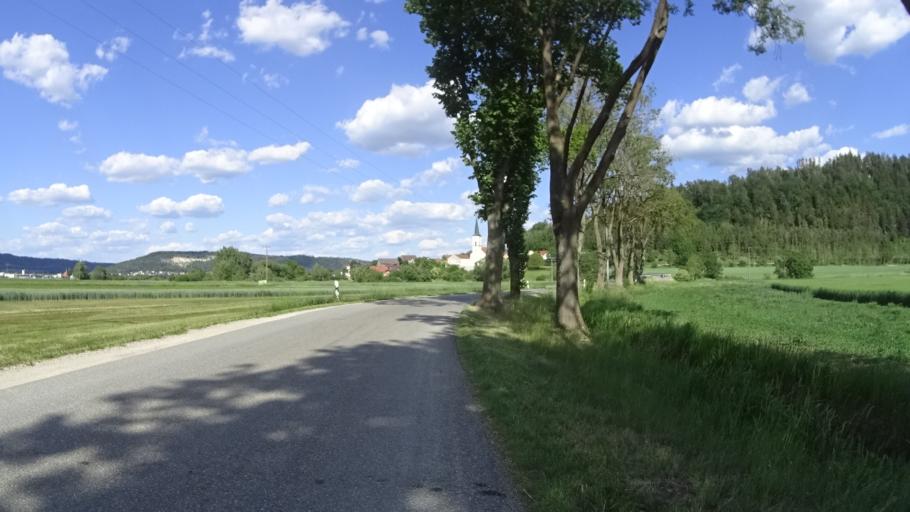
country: DE
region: Bavaria
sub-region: Upper Bavaria
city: Denkendorf
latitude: 49.0178
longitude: 11.4509
